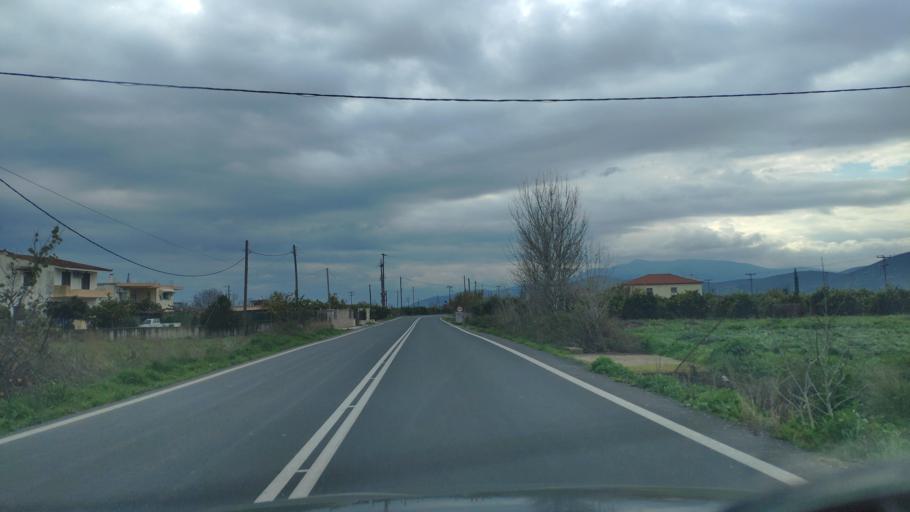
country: GR
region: Peloponnese
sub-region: Nomos Argolidos
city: Nea Kios
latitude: 37.5891
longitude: 22.7087
